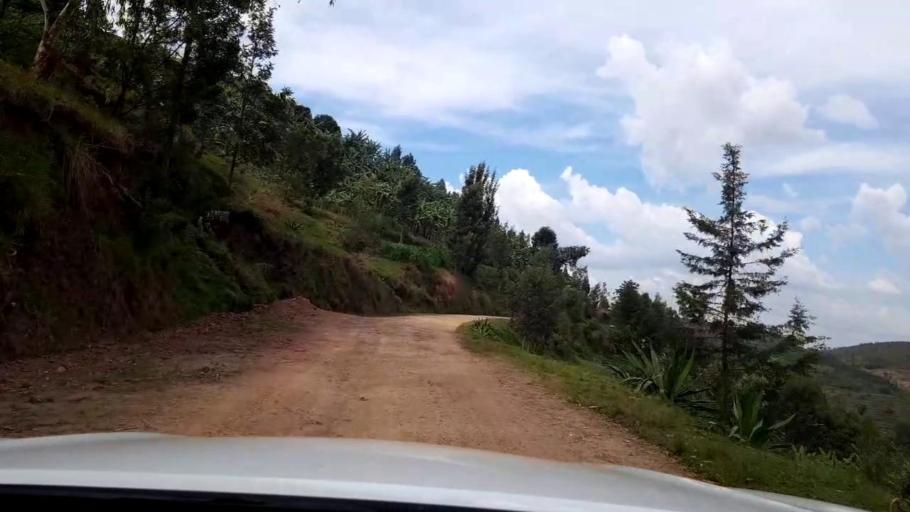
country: RW
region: Southern Province
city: Gitarama
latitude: -1.9920
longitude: 29.7078
